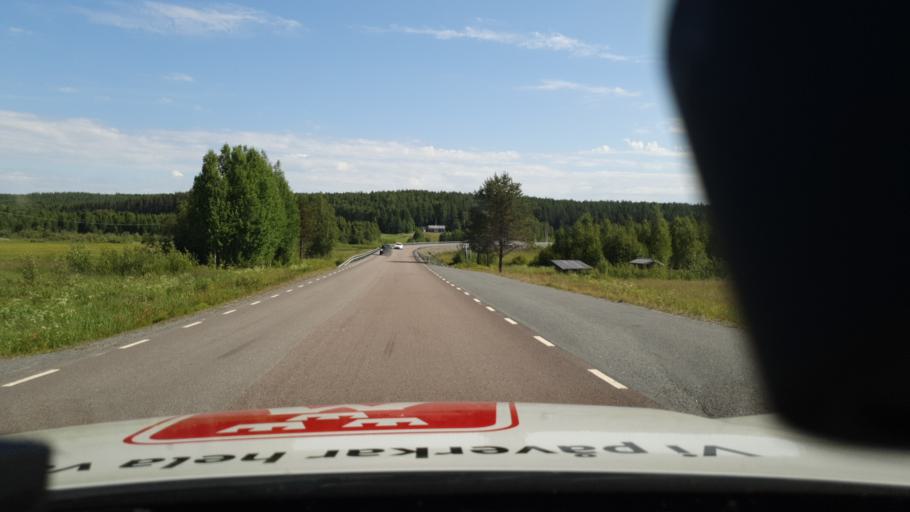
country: SE
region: Norrbotten
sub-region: Lulea Kommun
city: Sodra Sunderbyn
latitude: 65.8296
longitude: 21.9448
